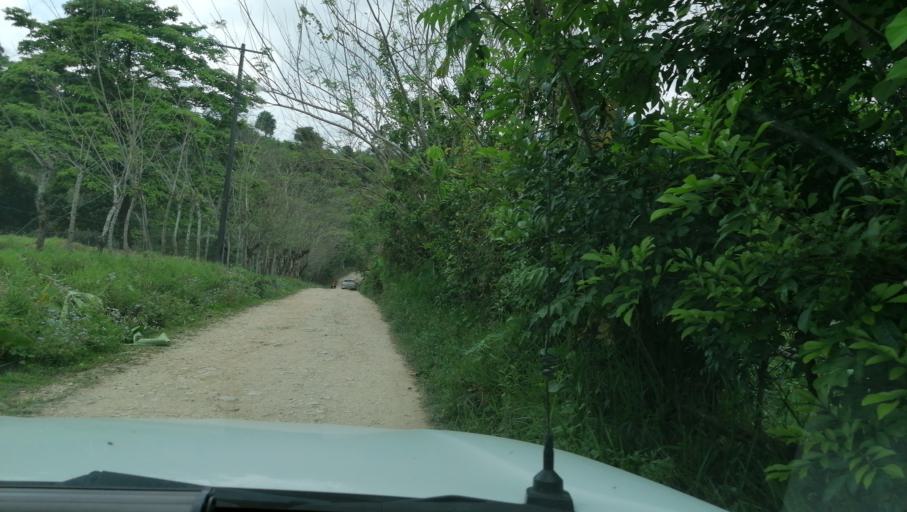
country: MX
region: Chiapas
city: Ocotepec
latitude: 17.2811
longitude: -93.2265
